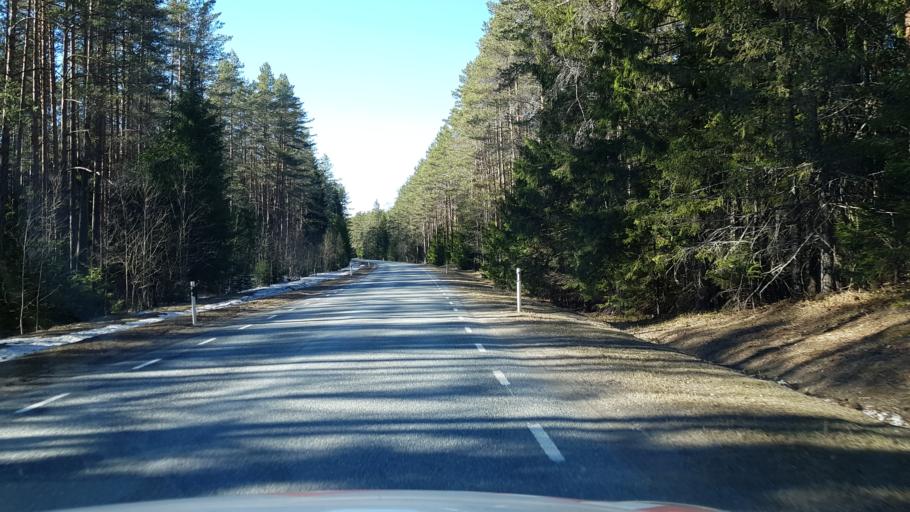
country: EE
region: Laeaene-Virumaa
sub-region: Vinni vald
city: Vinni
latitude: 59.2602
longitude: 26.6825
